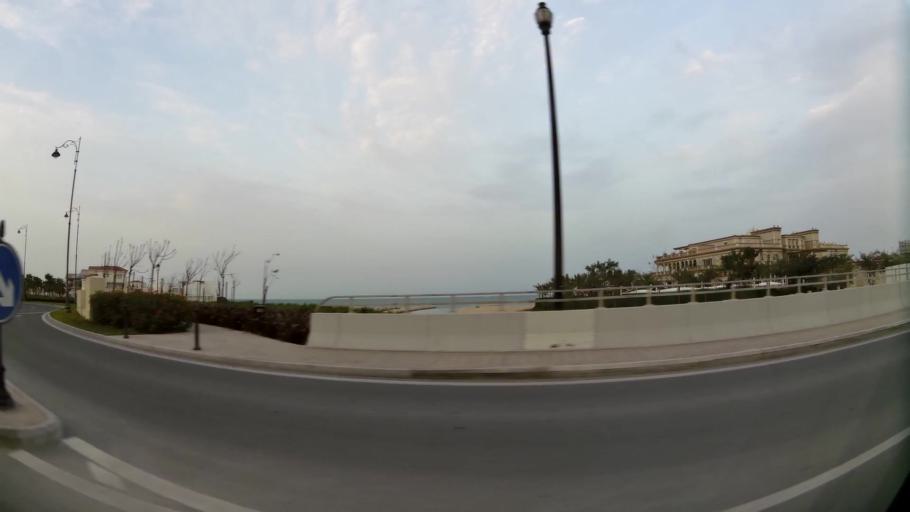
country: QA
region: Baladiyat ad Dawhah
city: Doha
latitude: 25.3690
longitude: 51.5623
